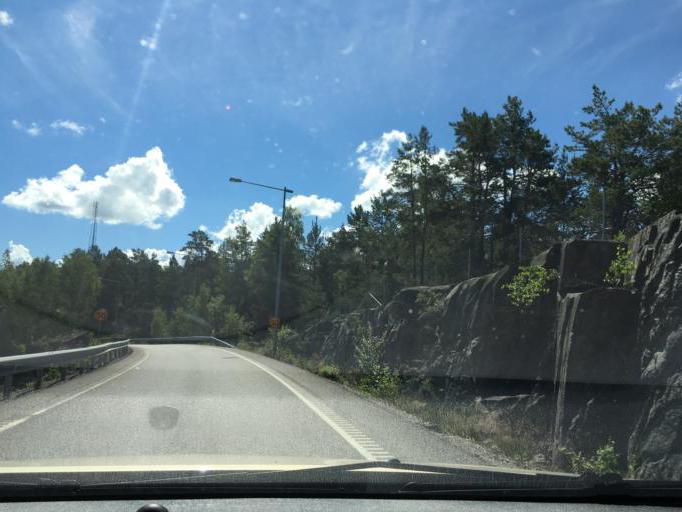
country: SE
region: Stockholm
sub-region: Nacka Kommun
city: Fisksatra
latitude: 59.2908
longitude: 18.2423
